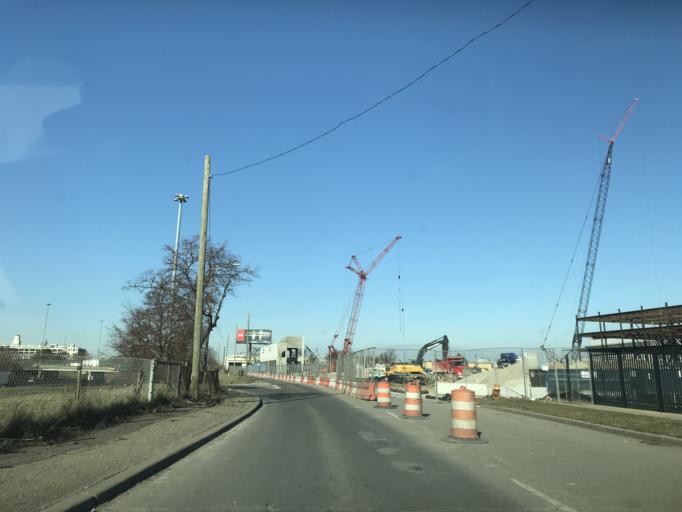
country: US
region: Michigan
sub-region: Wayne County
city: Hamtramck
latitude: 42.3630
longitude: -83.0545
